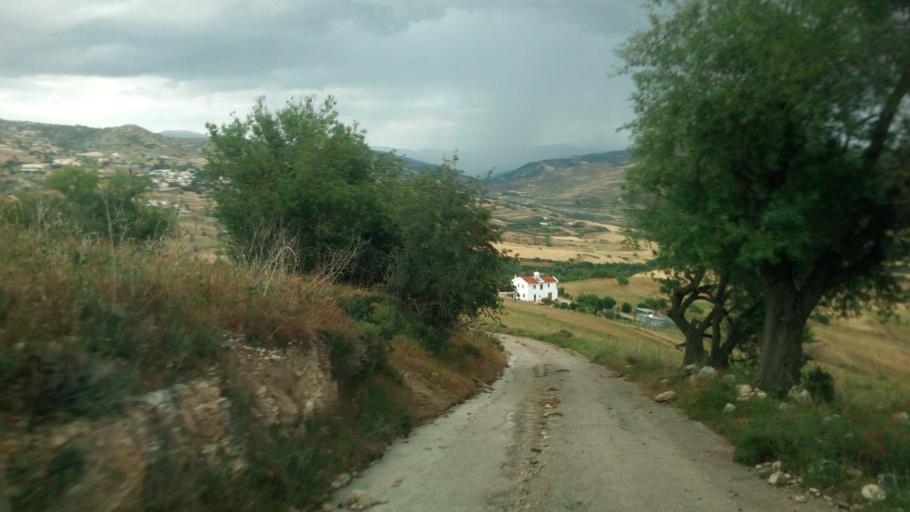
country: CY
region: Pafos
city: Mesogi
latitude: 34.7679
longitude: 32.5646
